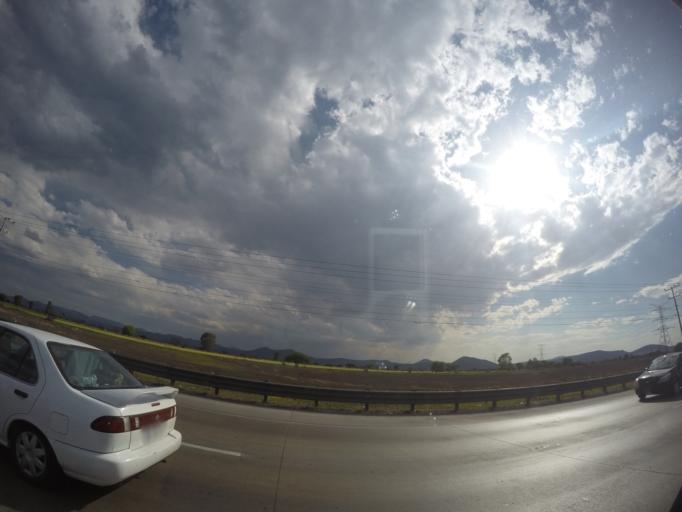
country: MX
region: Queretaro
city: El Sauz
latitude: 20.4744
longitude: -100.1087
